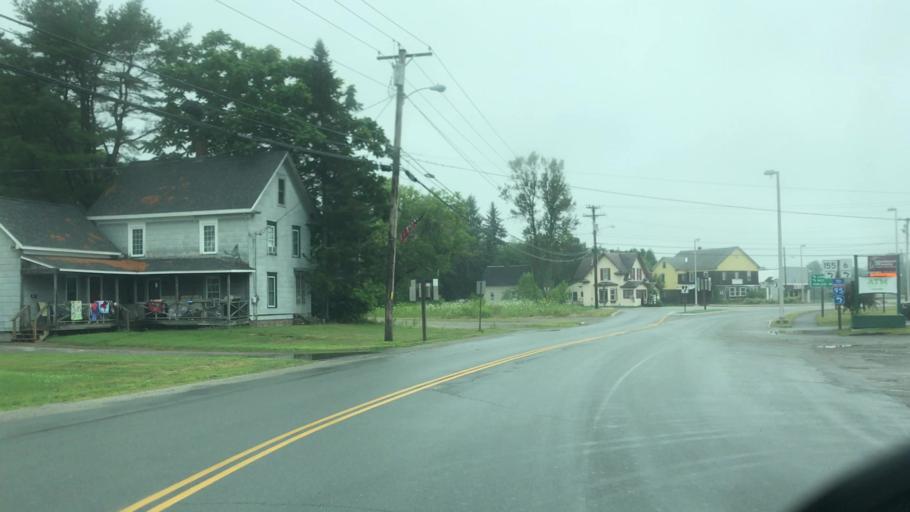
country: US
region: Maine
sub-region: Penobscot County
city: Howland
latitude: 45.2376
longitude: -68.6602
